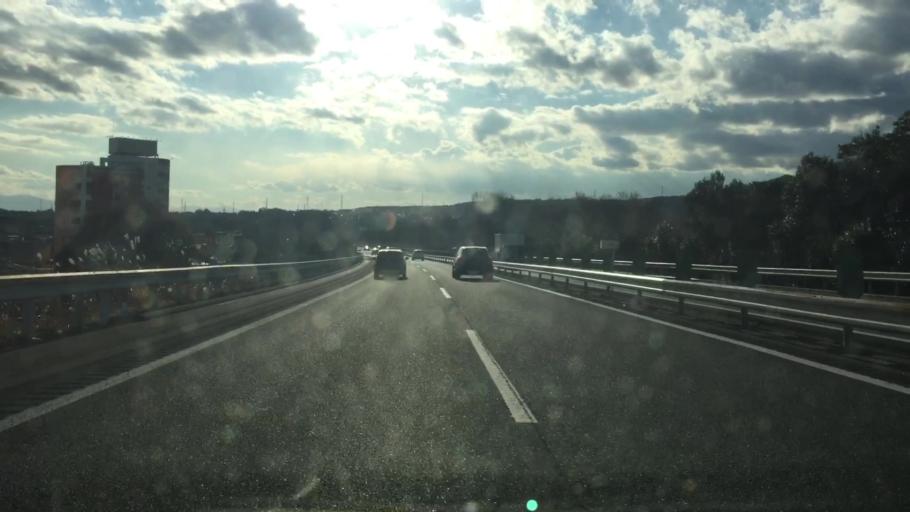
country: JP
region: Gunma
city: Shibukawa
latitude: 36.4797
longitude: 139.0200
